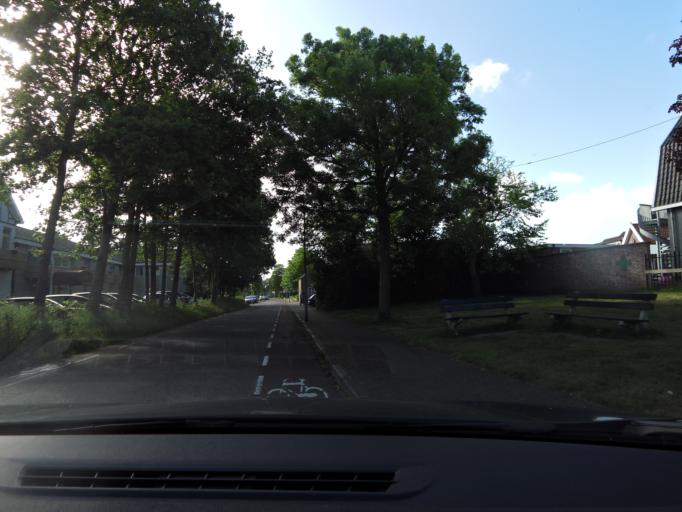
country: NL
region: Zeeland
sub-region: Schouwen-Duiveland
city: Renesse
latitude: 51.7337
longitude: 3.7756
